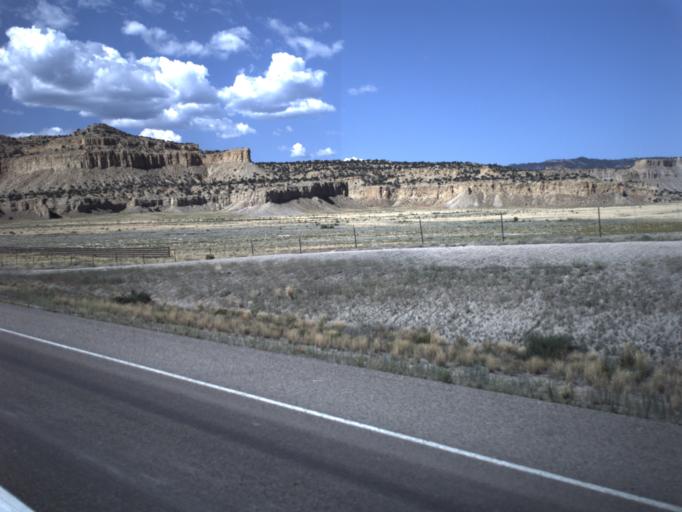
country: US
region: Utah
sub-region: Emery County
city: Ferron
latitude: 38.8512
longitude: -111.3078
